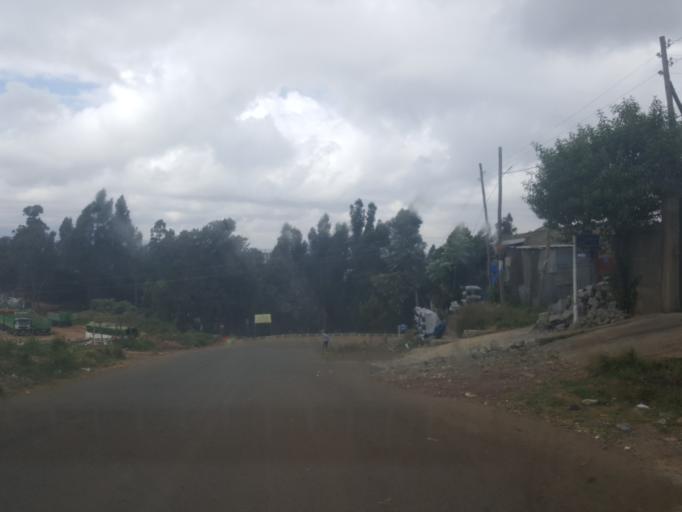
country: ET
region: Adis Abeba
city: Addis Ababa
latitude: 9.0676
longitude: 38.7406
